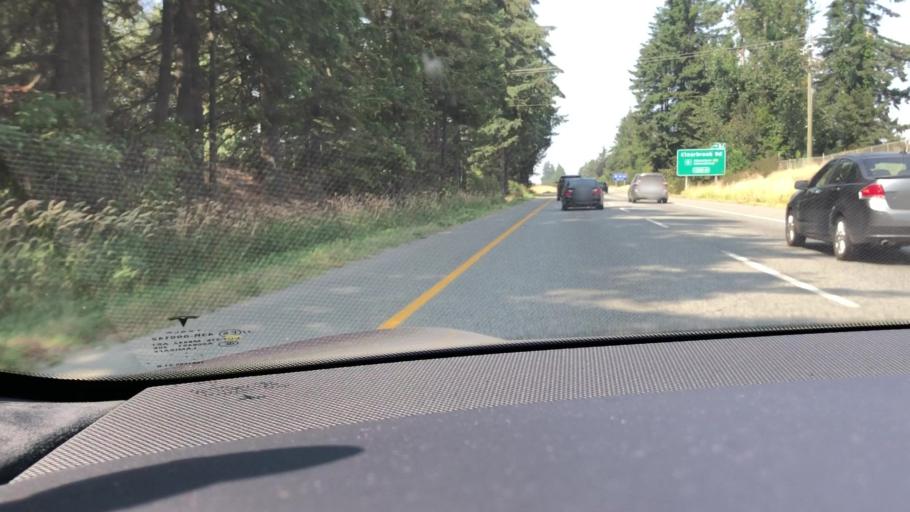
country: US
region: Washington
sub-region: Whatcom County
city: Sumas
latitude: 49.0356
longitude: -122.3145
